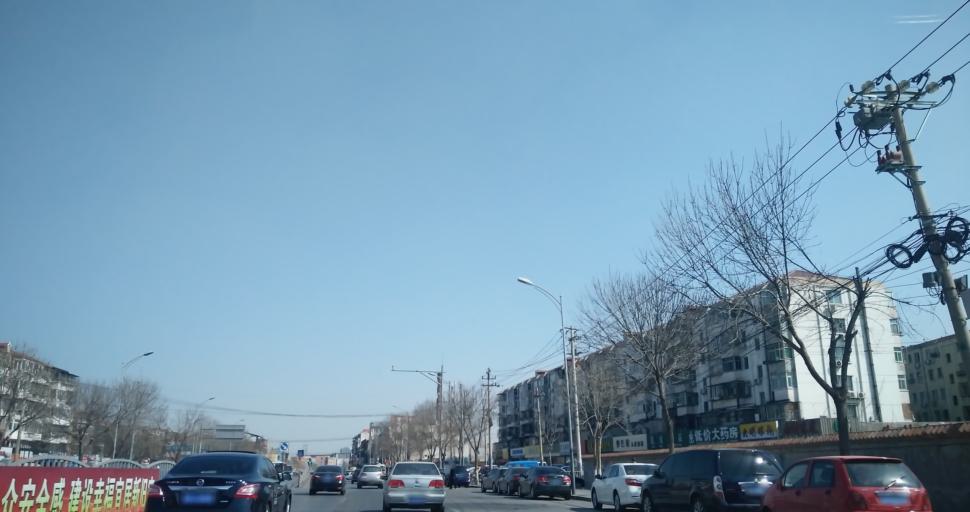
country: CN
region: Beijing
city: Jiugong
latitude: 39.8024
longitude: 116.4243
